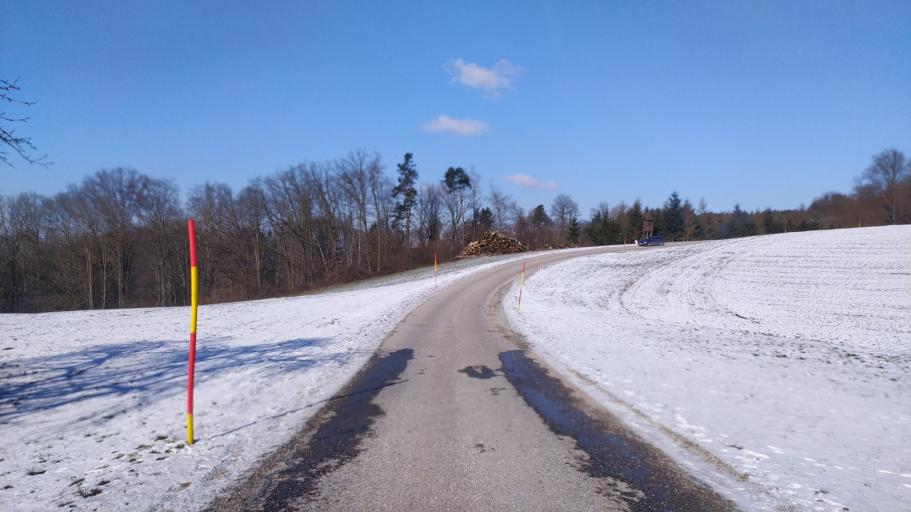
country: AT
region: Upper Austria
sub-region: Politischer Bezirk Urfahr-Umgebung
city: Ottensheim
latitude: 48.3249
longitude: 14.2139
